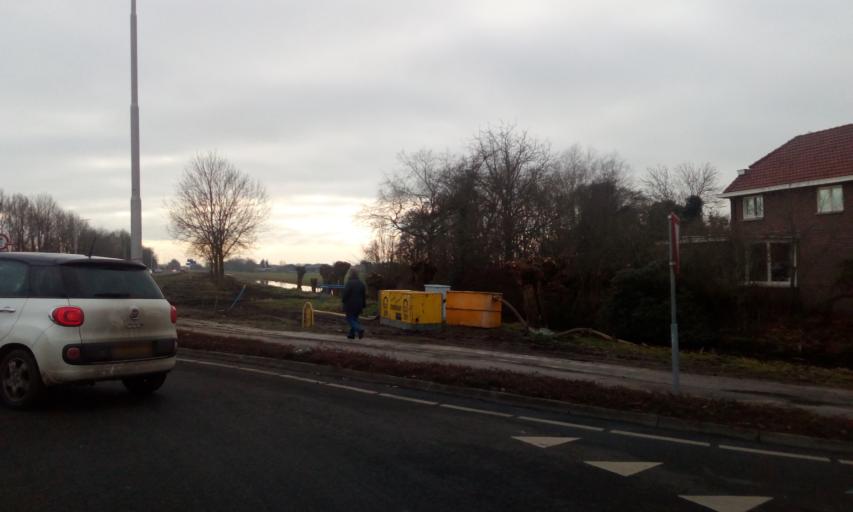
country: NL
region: South Holland
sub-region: Molenwaard
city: Liesveld
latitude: 51.9368
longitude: 4.7793
